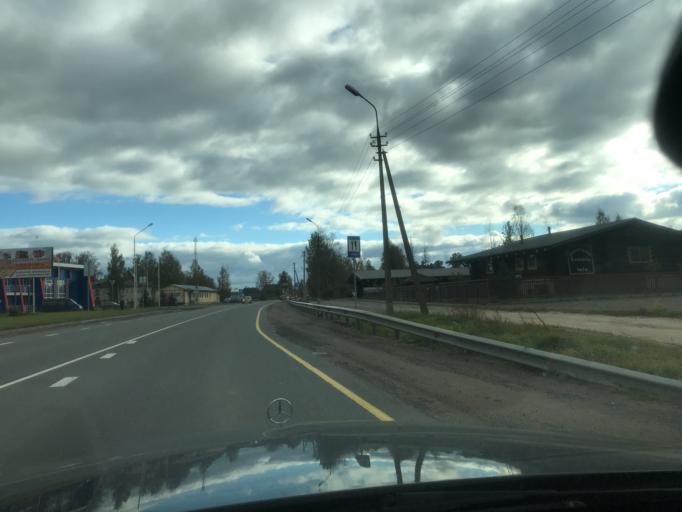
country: RU
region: Pskov
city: Opochka
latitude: 56.7102
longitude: 28.6909
